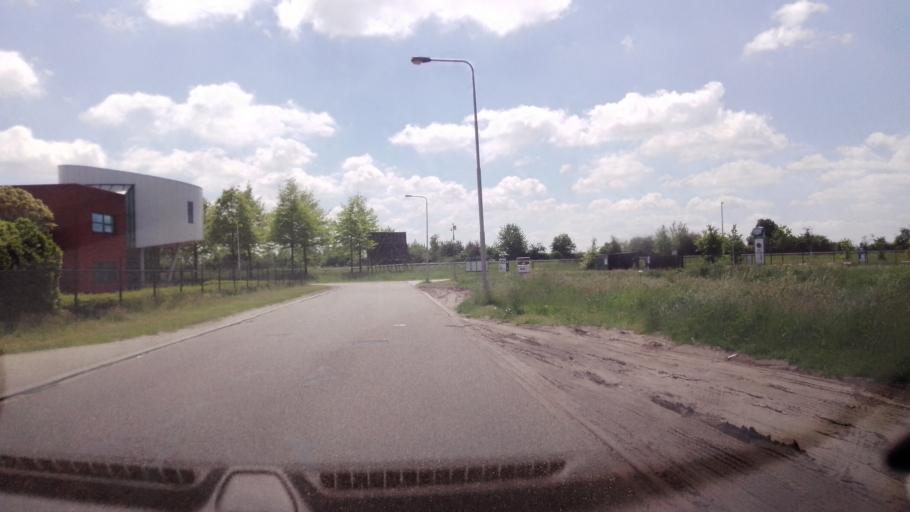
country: NL
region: Limburg
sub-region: Gemeente Peel en Maas
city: Maasbree
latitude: 51.3948
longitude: 6.0740
